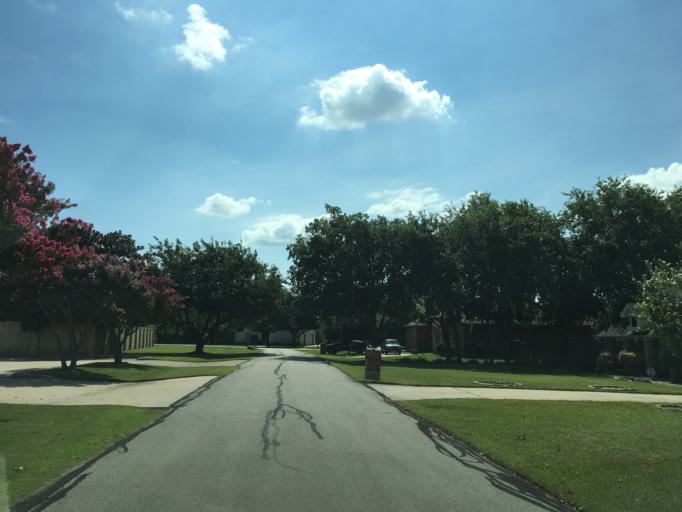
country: US
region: Texas
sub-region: Dallas County
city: Farmers Branch
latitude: 32.9140
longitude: -96.8799
